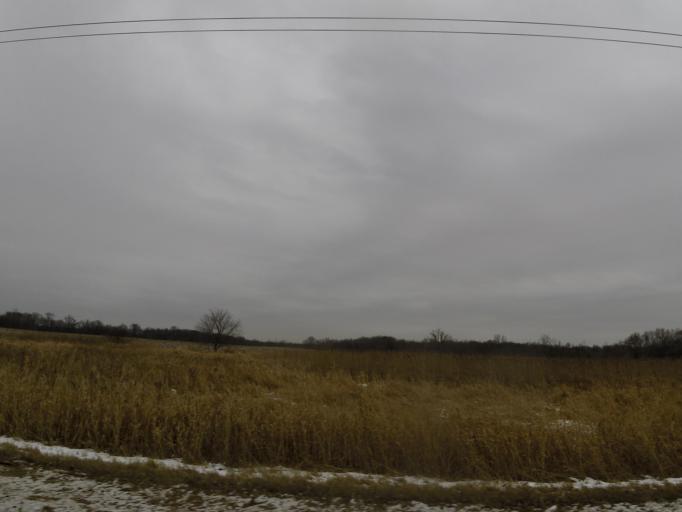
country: US
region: Minnesota
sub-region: Hennepin County
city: Medina
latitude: 45.0408
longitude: -93.5686
